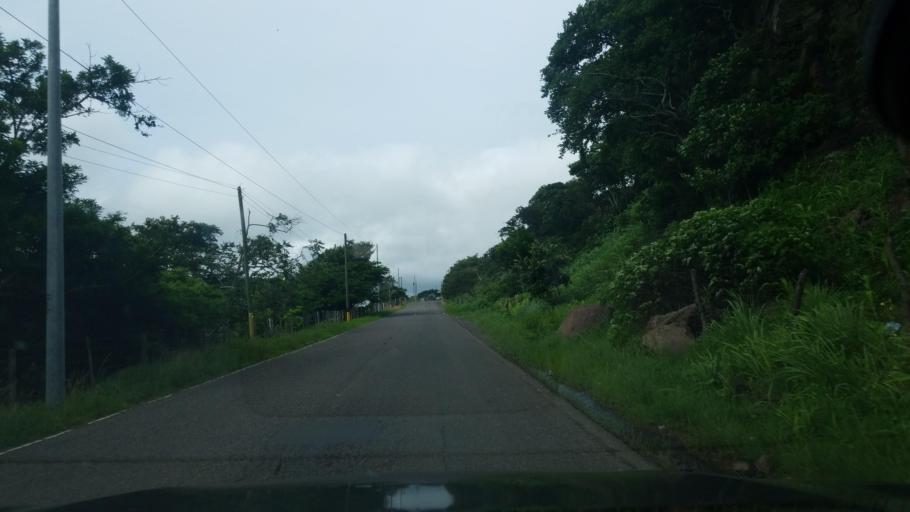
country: HN
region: Choluteca
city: San Marcos de Colon
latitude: 13.3714
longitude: -86.9197
